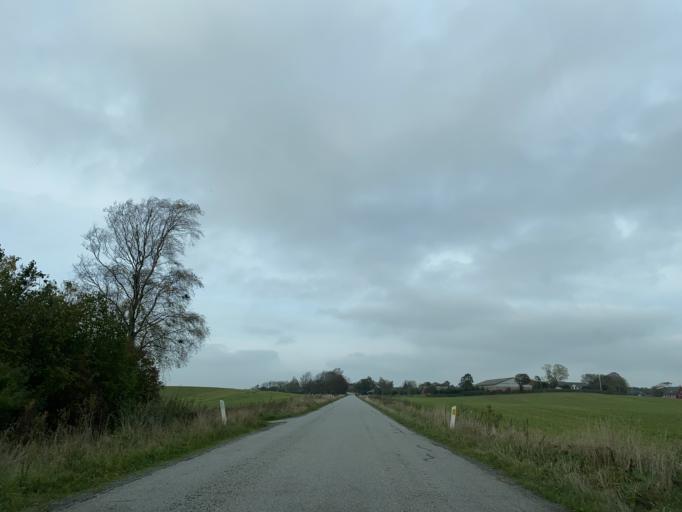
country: DK
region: South Denmark
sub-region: Haderslev Kommune
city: Starup
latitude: 55.1839
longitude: 9.5166
